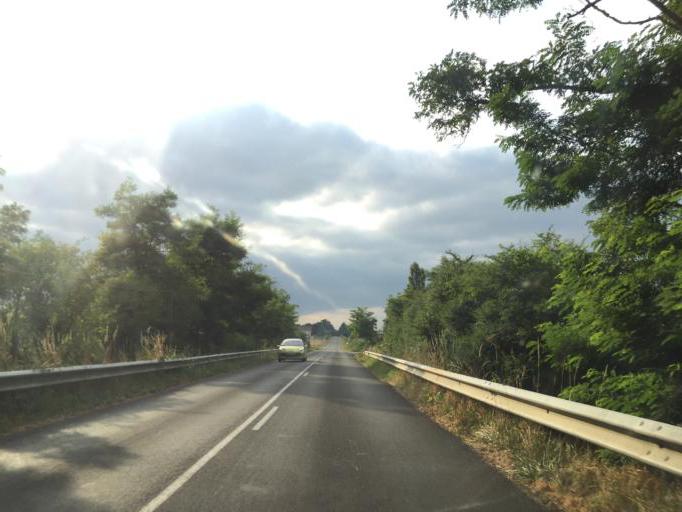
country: FR
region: Auvergne
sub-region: Departement de l'Allier
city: Yzeure
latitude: 46.5474
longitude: 3.3742
